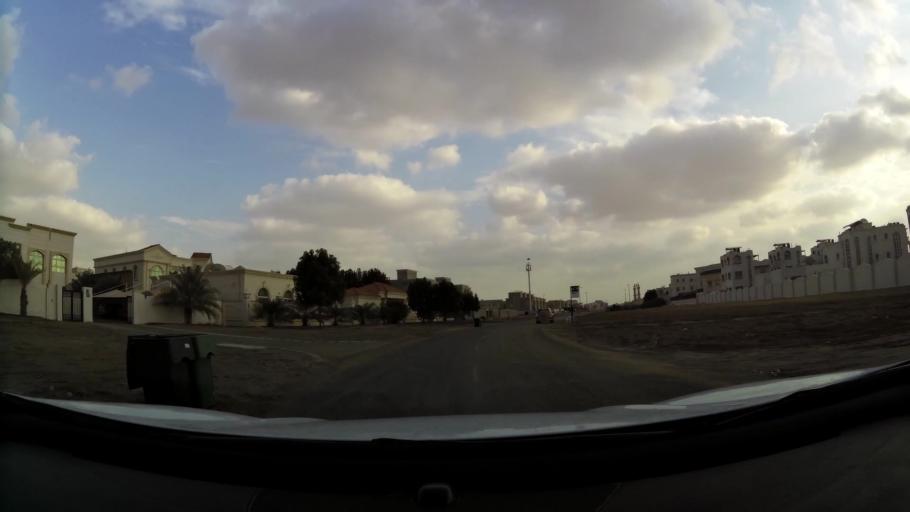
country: AE
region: Abu Dhabi
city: Abu Dhabi
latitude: 24.3584
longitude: 54.5585
